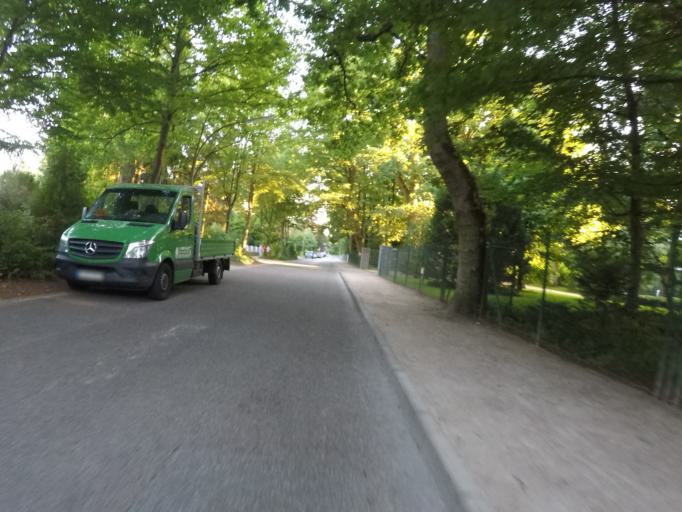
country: DE
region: Hamburg
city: Poppenbuettel
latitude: 53.6642
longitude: 10.0980
